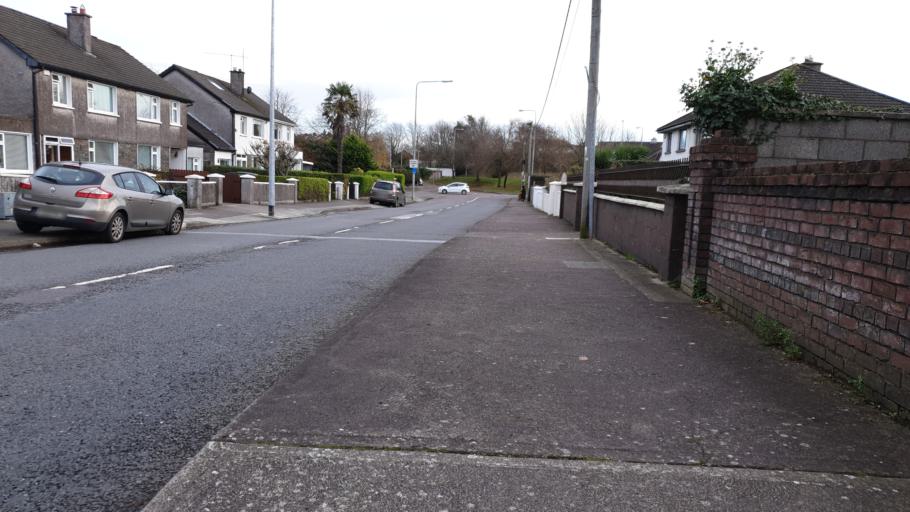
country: IE
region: Munster
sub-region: County Cork
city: Cork
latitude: 51.8940
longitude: -8.4097
